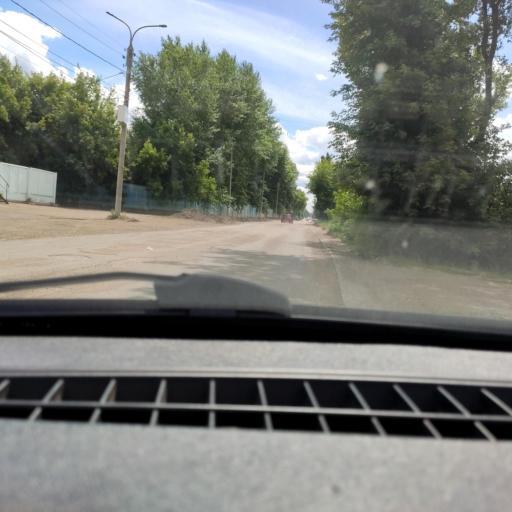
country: RU
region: Bashkortostan
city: Sterlitamak
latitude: 53.6514
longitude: 55.9402
